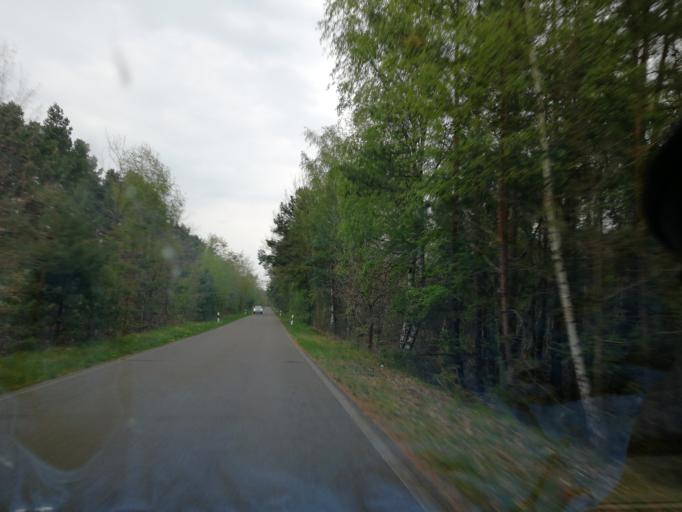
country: DE
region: Brandenburg
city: Calau
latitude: 51.7996
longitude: 13.8848
